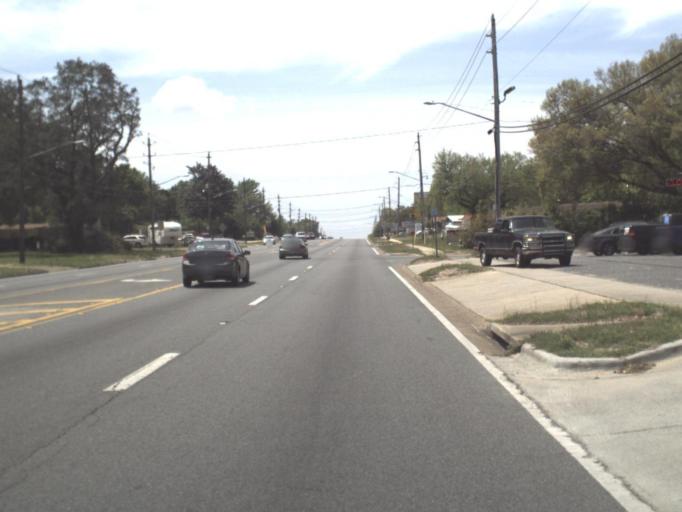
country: US
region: Florida
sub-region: Escambia County
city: Brent
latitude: 30.4632
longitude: -87.2632
